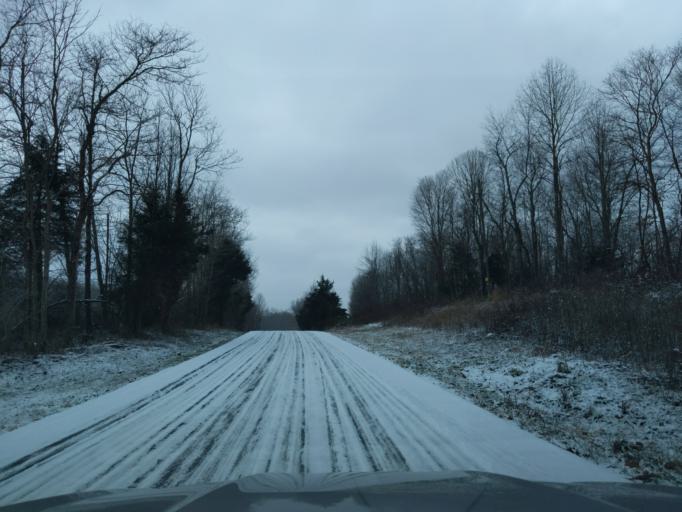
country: US
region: Indiana
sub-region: Decatur County
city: Westport
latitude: 39.2111
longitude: -85.5207
